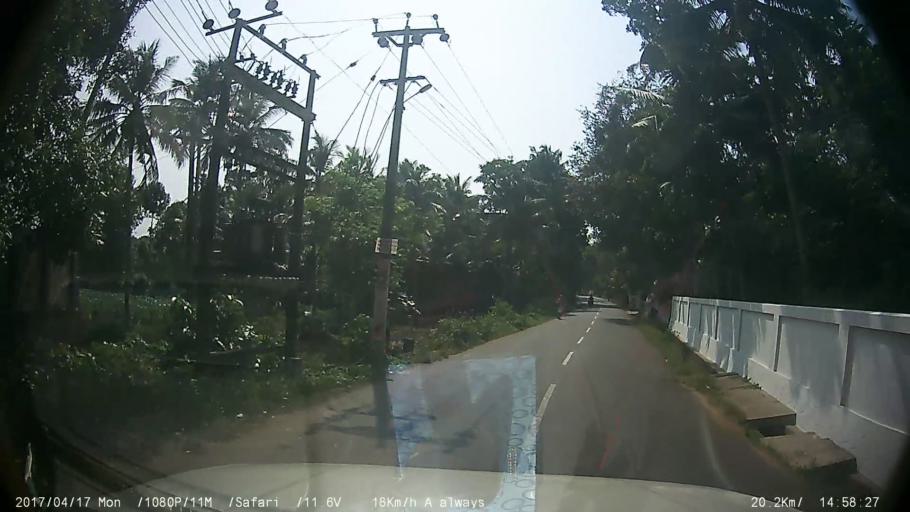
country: IN
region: Kerala
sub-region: Ernakulam
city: Piravam
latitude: 9.8356
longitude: 76.4986
